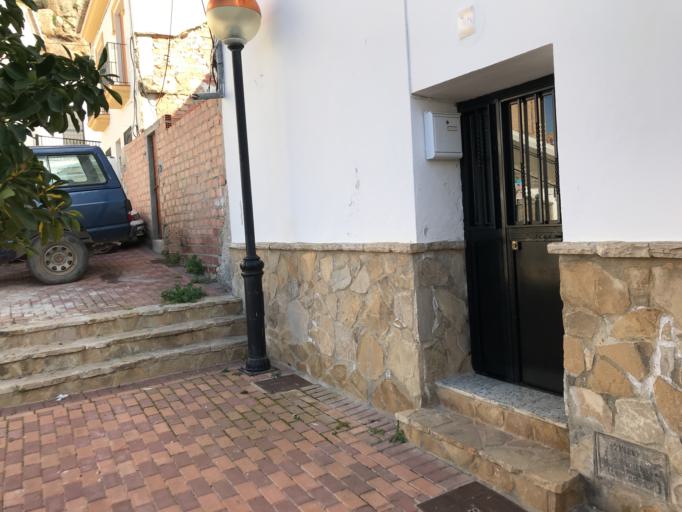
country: ES
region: Andalusia
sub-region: Provincia de Malaga
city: Ardales
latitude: 36.8762
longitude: -4.8456
